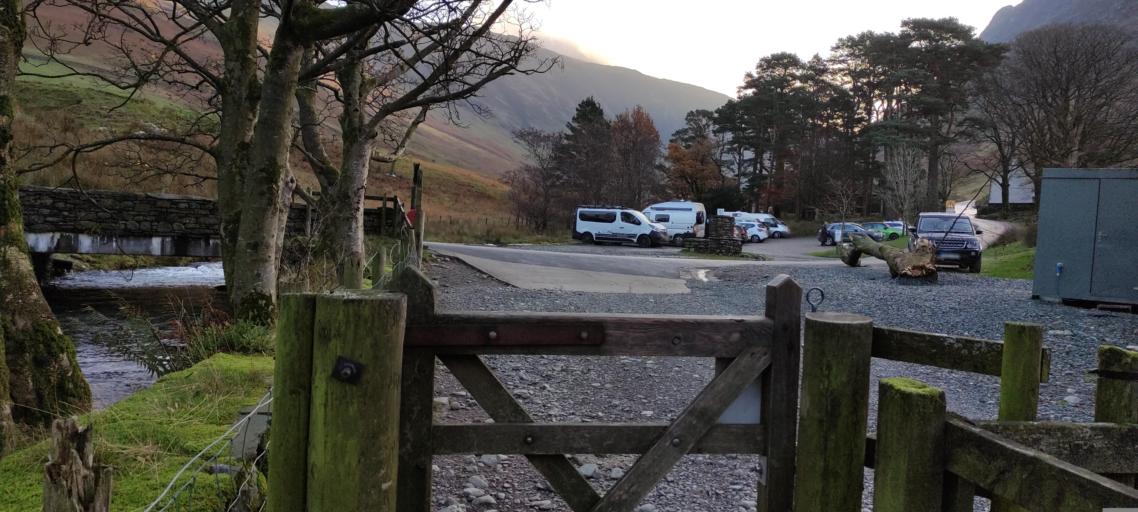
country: GB
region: England
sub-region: Cumbria
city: Keswick
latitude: 54.5238
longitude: -3.2466
